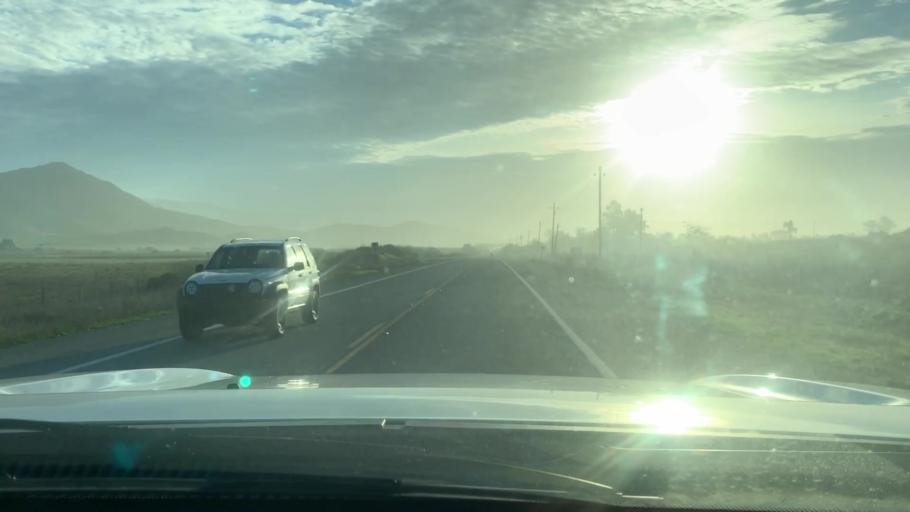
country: US
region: California
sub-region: San Luis Obispo County
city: San Luis Obispo
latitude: 35.2800
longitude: -120.7208
